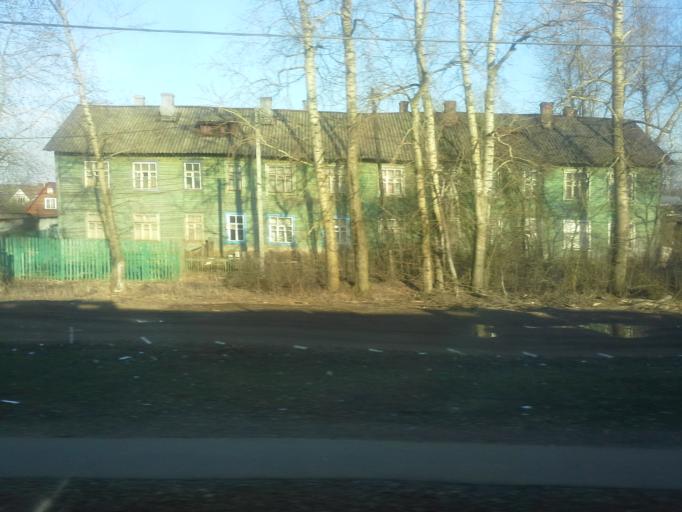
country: RU
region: Moskovskaya
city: Nekrasovskiy
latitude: 56.0914
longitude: 37.5046
